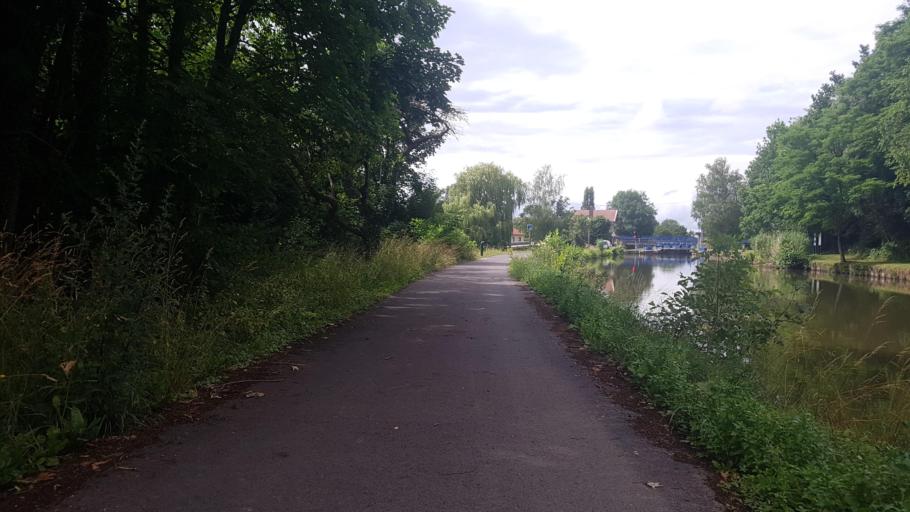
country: FR
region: Lorraine
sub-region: Departement de la Moselle
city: Dieuze
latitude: 48.6770
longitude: 6.7902
